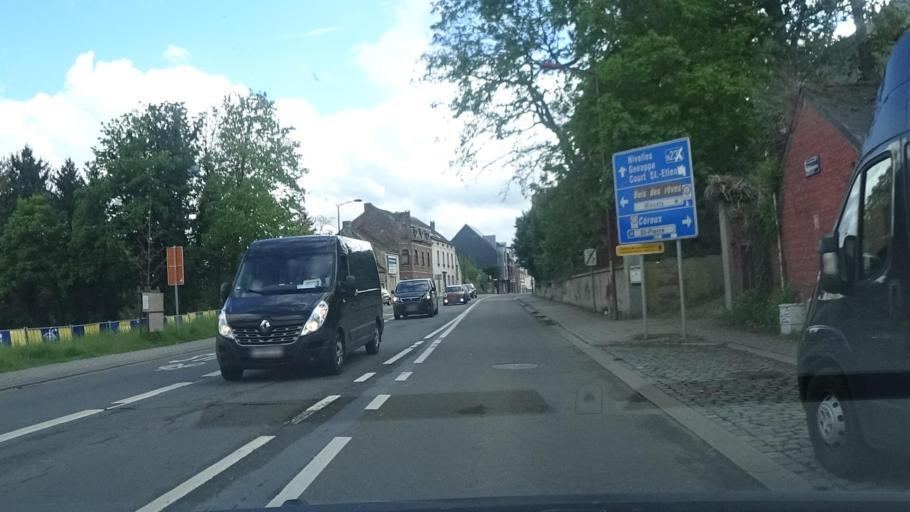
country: BE
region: Wallonia
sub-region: Province du Brabant Wallon
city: Ottignies
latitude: 50.6630
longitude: 4.5649
